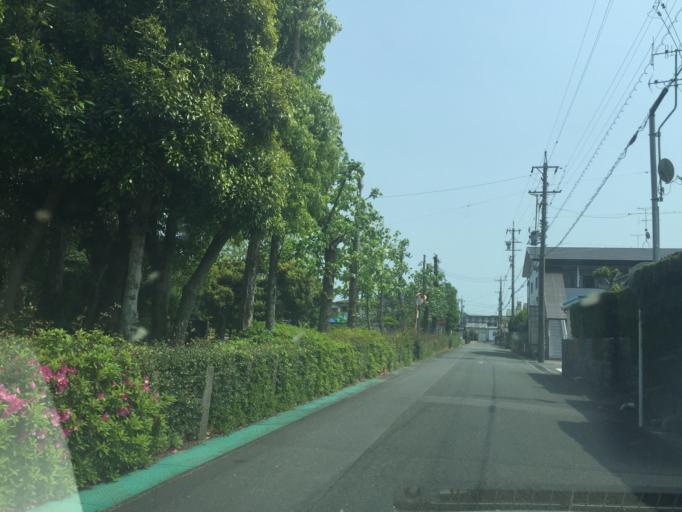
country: JP
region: Shizuoka
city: Kakegawa
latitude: 34.7752
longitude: 138.0290
